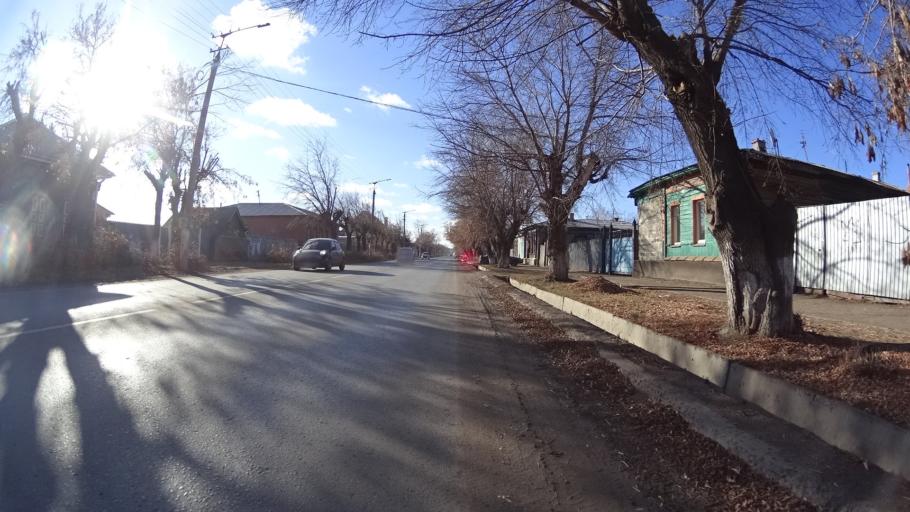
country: RU
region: Chelyabinsk
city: Troitsk
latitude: 54.0801
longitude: 61.5491
